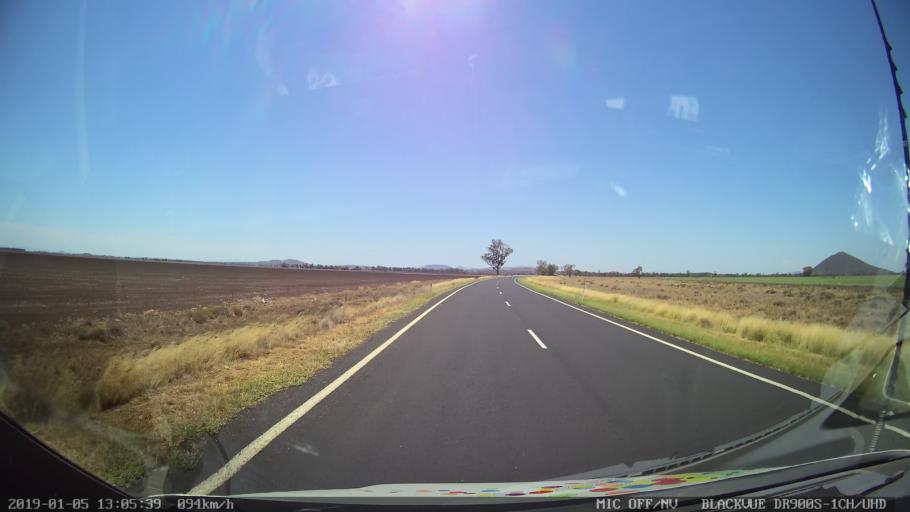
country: AU
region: New South Wales
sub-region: Gunnedah
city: Gunnedah
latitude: -31.0948
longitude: 149.8564
